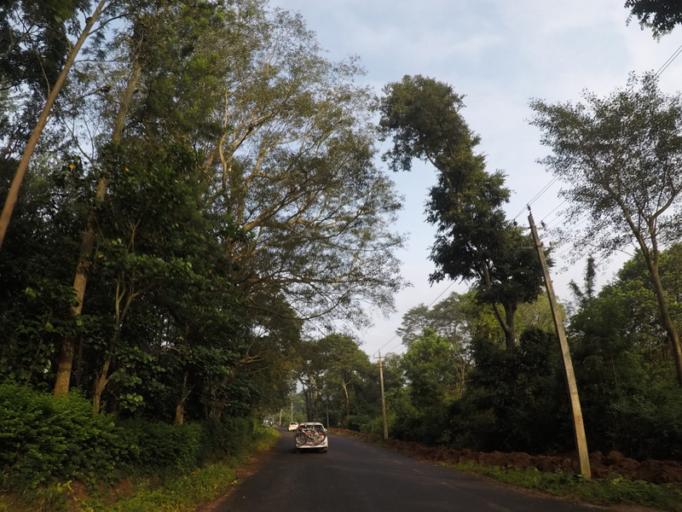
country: IN
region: Karnataka
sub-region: Chikmagalur
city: Chikmagalur
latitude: 13.4382
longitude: 75.8063
